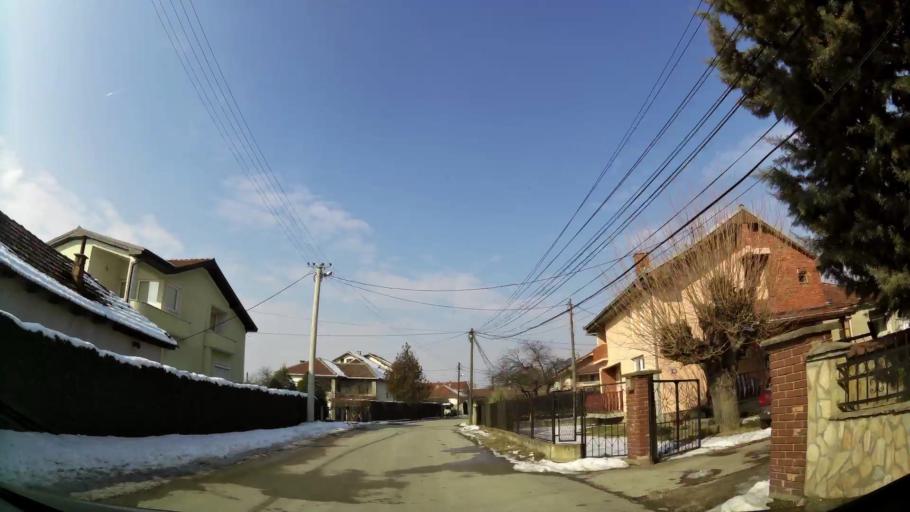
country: MK
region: Suto Orizari
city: Suto Orizare
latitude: 42.0260
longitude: 21.3773
